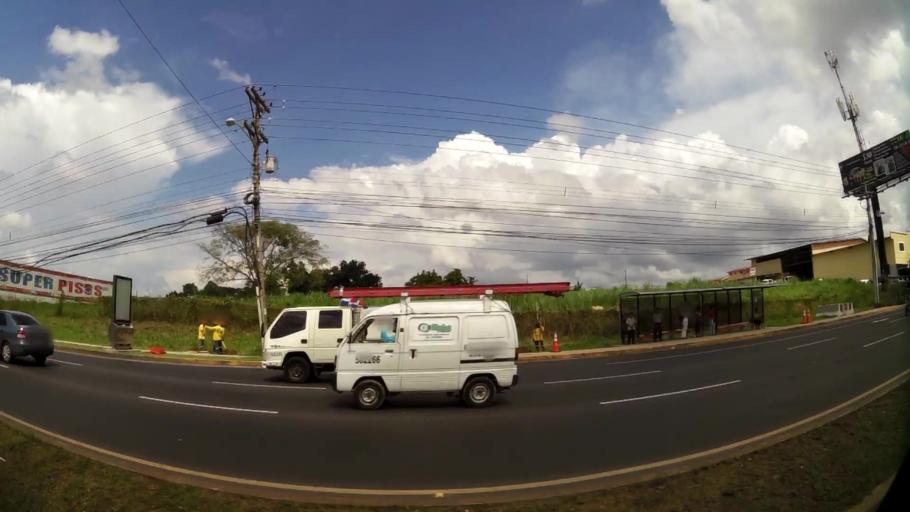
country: PA
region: Panama
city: San Miguelito
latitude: 9.0518
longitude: -79.4452
